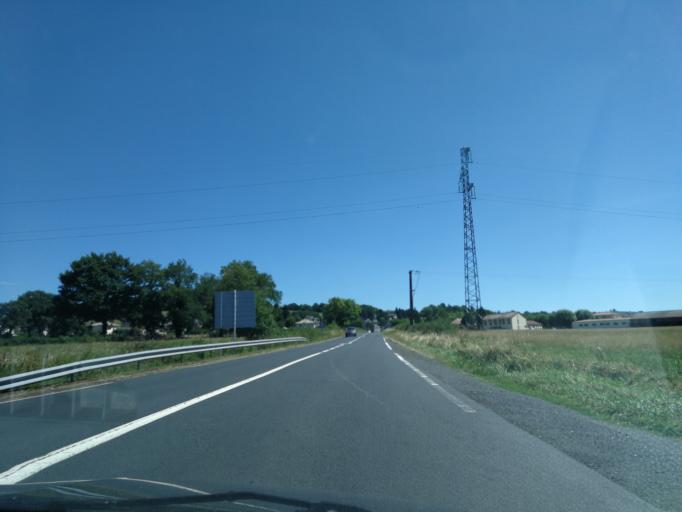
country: FR
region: Auvergne
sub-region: Departement du Cantal
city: Naucelles
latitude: 44.9361
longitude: 2.4105
